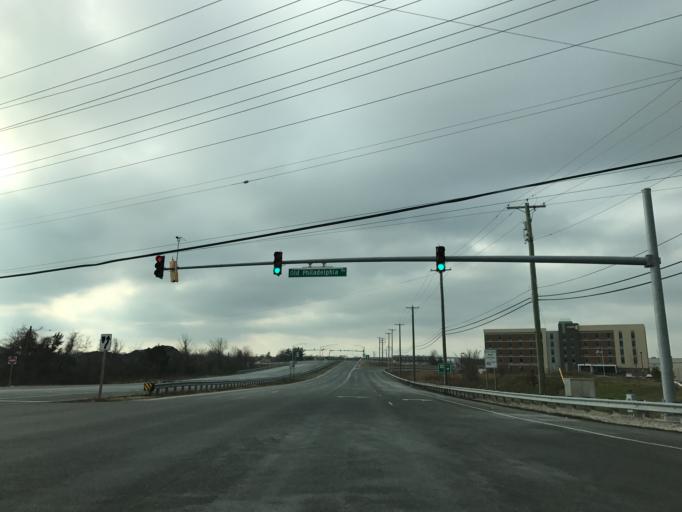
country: US
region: Maryland
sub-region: Harford County
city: Aberdeen
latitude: 39.4924
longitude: -76.1797
